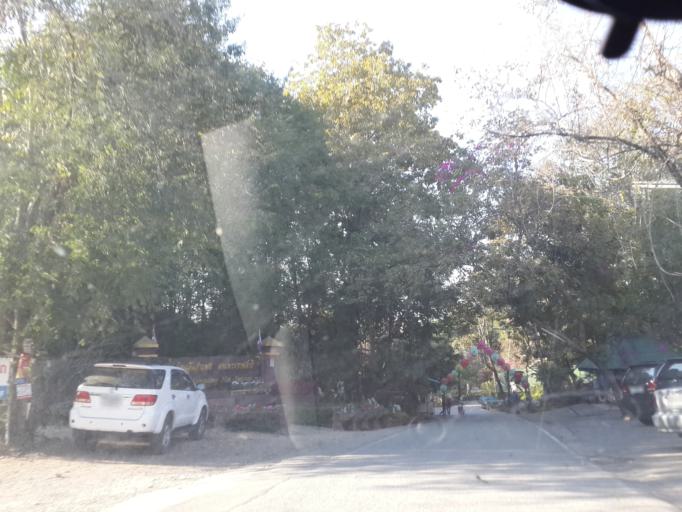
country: TH
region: Chiang Mai
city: Mae On
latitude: 18.8144
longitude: 99.2297
